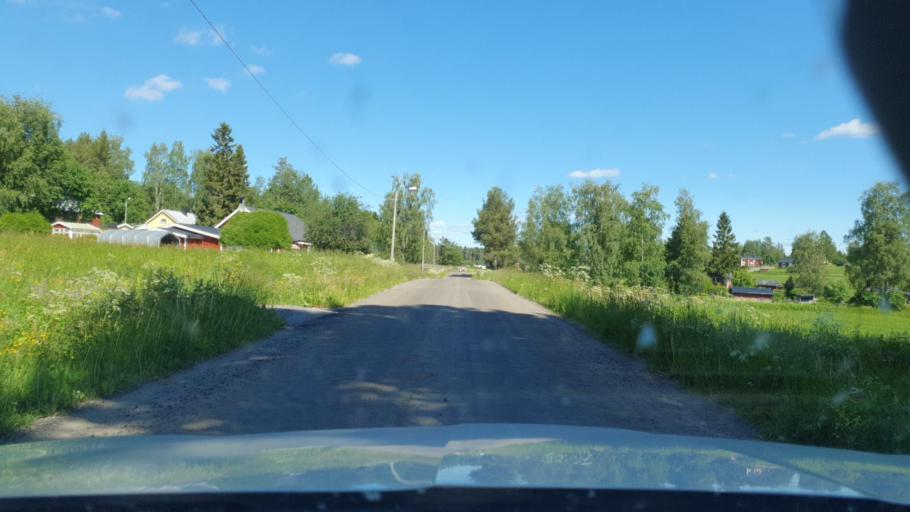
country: SE
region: Vaesterbotten
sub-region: Skelleftea Kommun
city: Byske
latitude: 65.1154
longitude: 21.2036
